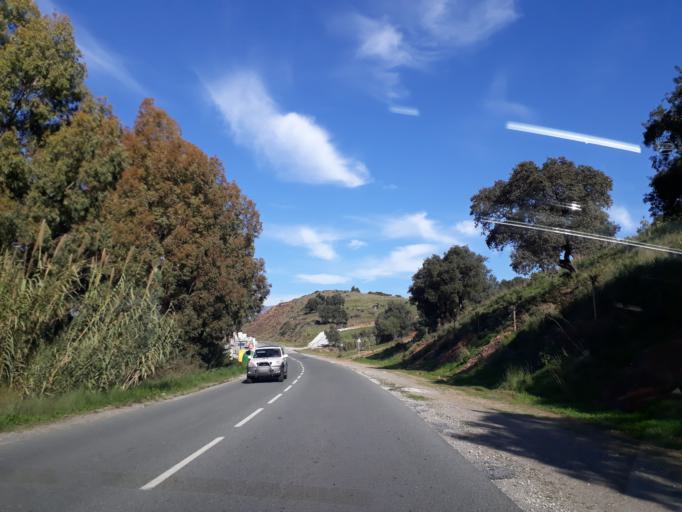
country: ES
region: Andalusia
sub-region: Provincia de Malaga
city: Fuengirola
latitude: 36.5166
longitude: -4.6851
